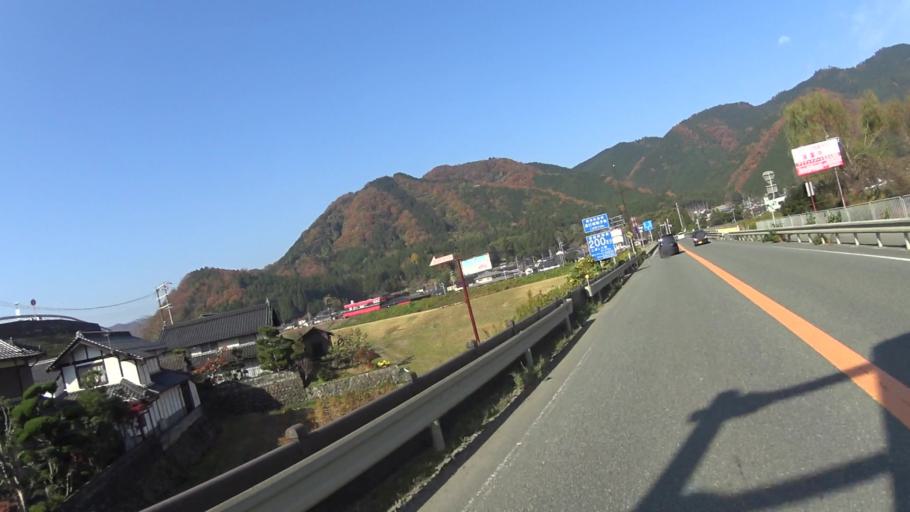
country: JP
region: Kyoto
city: Fukuchiyama
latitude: 35.3328
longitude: 135.0996
